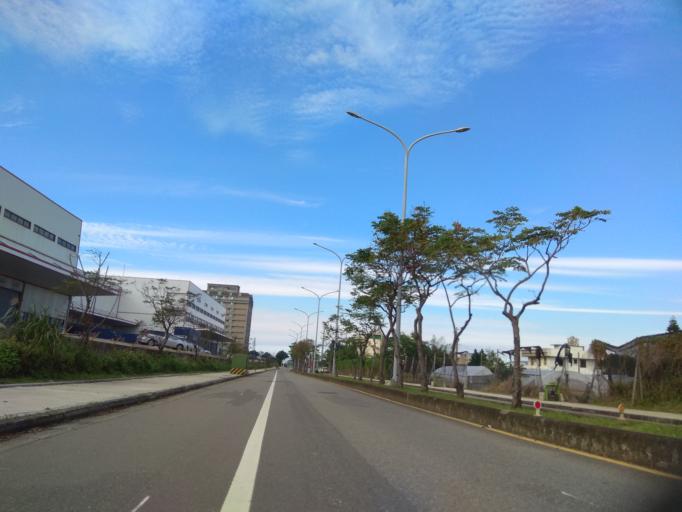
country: TW
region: Taiwan
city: Taoyuan City
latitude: 25.0596
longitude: 121.1791
